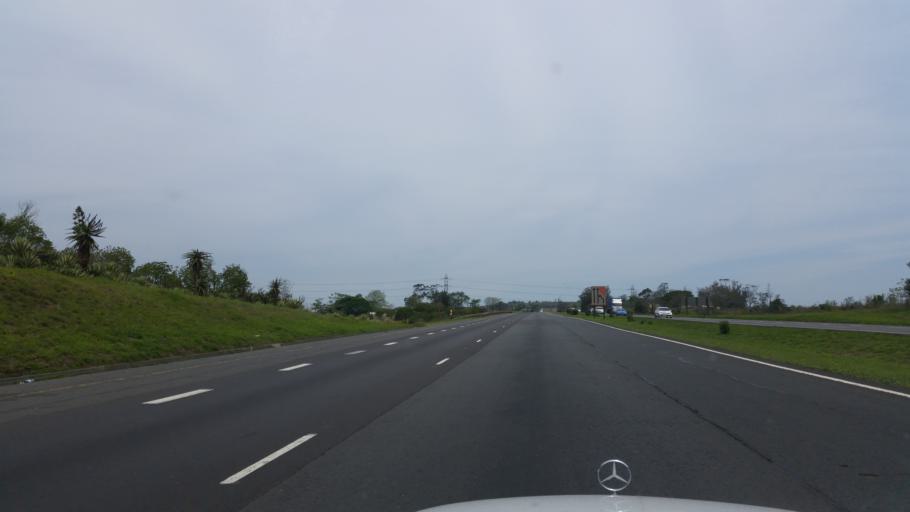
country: ZA
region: KwaZulu-Natal
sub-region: uMgungundlovu District Municipality
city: Camperdown
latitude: -29.6940
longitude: 30.4844
